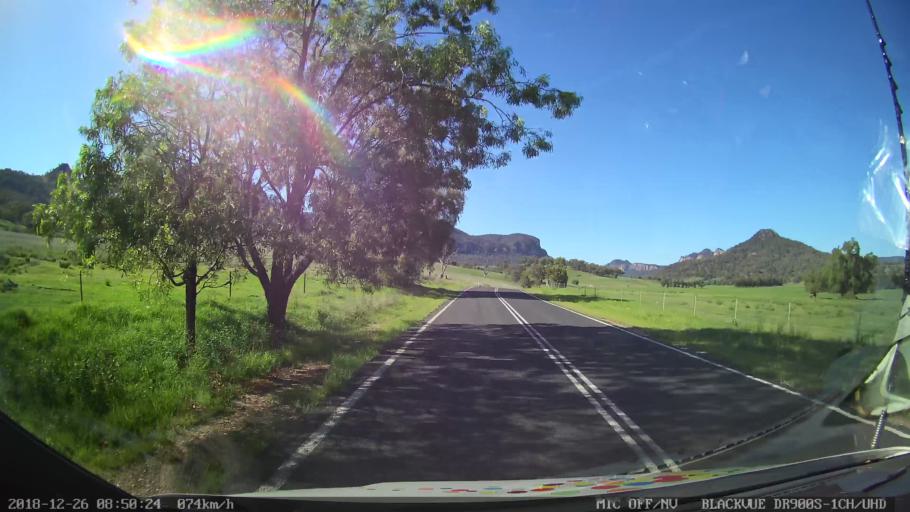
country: AU
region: New South Wales
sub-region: Mid-Western Regional
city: Kandos
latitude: -32.5750
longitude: 150.0951
